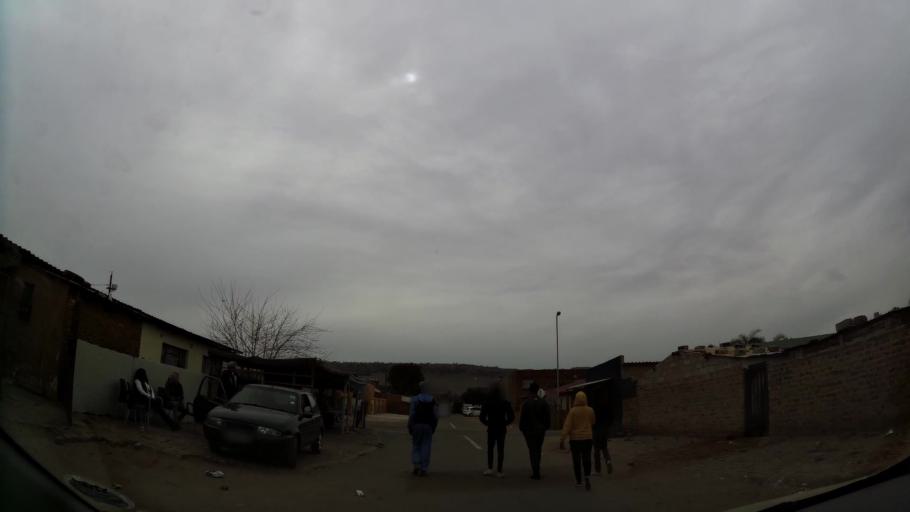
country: ZA
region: Gauteng
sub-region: City of Tshwane Metropolitan Municipality
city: Pretoria
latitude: -25.7072
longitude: 28.3338
